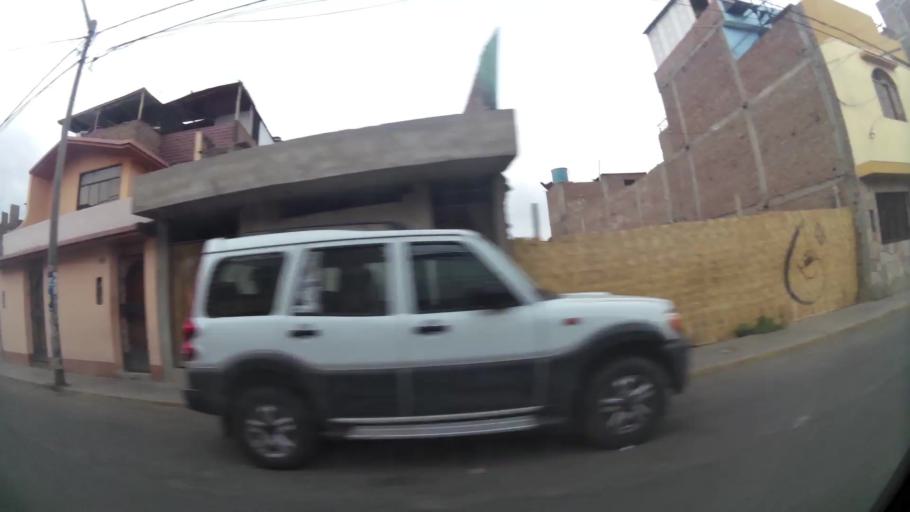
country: PE
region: La Libertad
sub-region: Provincia de Trujillo
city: Trujillo
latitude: -8.1025
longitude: -79.0222
